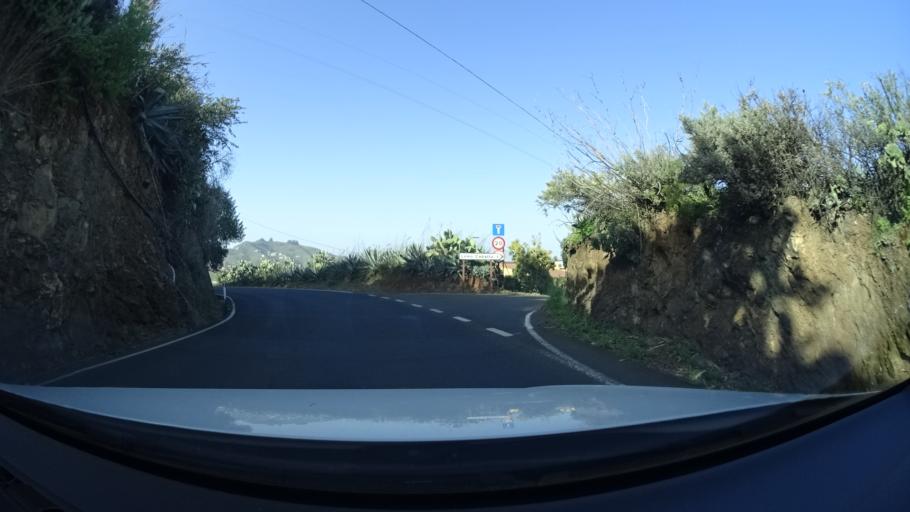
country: ES
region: Canary Islands
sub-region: Provincia de Las Palmas
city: Vega de San Mateo
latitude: 28.0135
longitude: -15.5359
